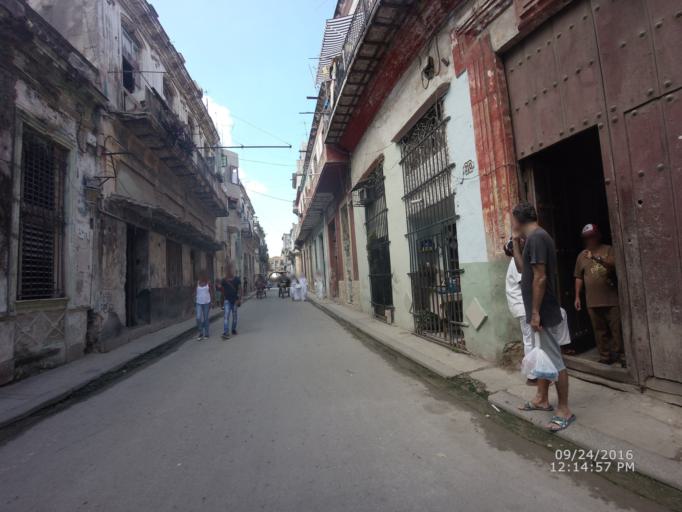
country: CU
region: La Habana
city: La Habana Vieja
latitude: 23.1326
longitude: -82.3510
